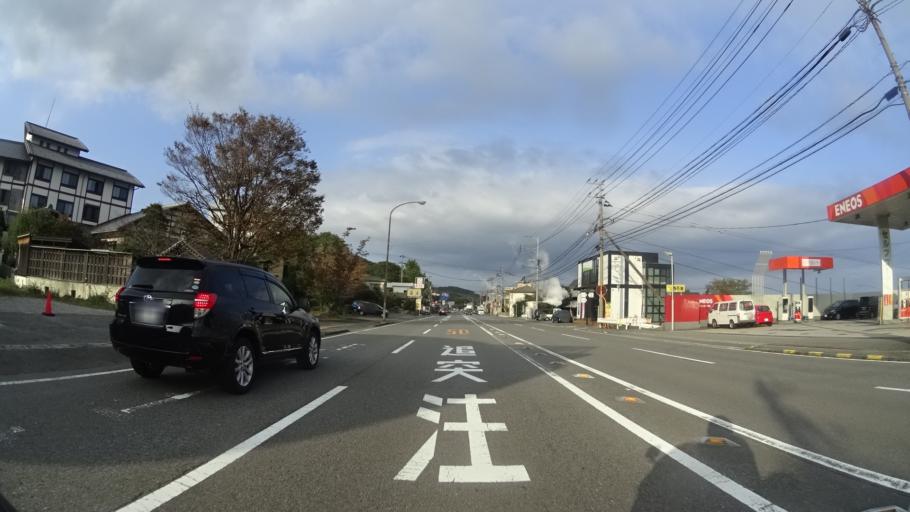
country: JP
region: Oita
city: Beppu
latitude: 33.3074
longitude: 131.4623
